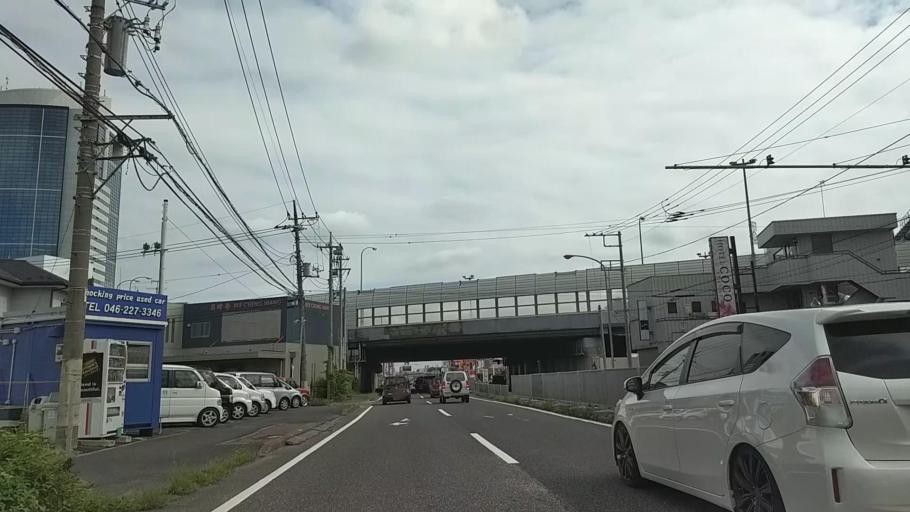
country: JP
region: Kanagawa
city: Atsugi
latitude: 35.4251
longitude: 139.3583
